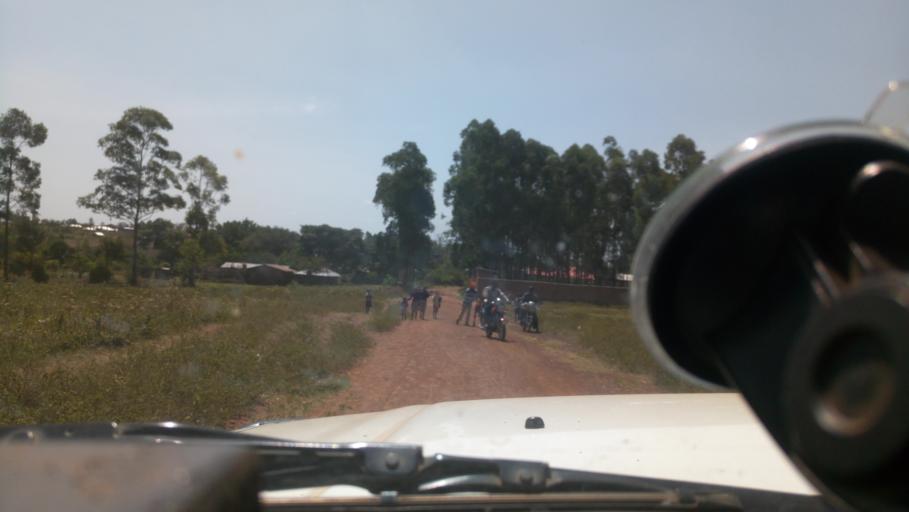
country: KE
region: Migori
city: Kihancha
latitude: -1.1915
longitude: 34.6117
